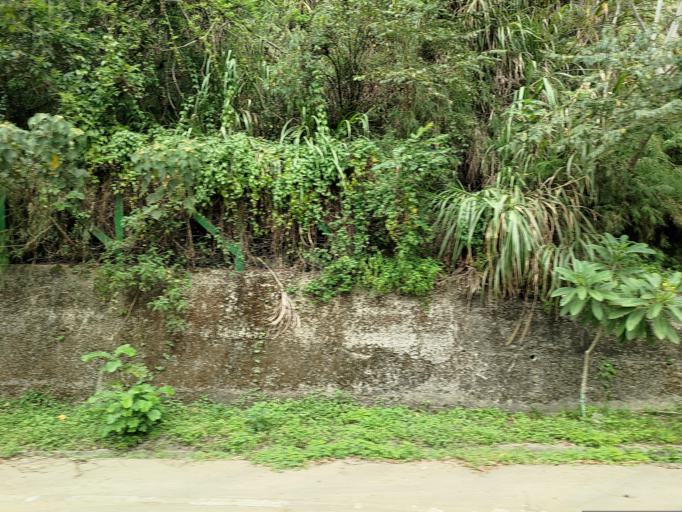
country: TW
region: Taiwan
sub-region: Miaoli
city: Miaoli
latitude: 24.6004
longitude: 121.0328
